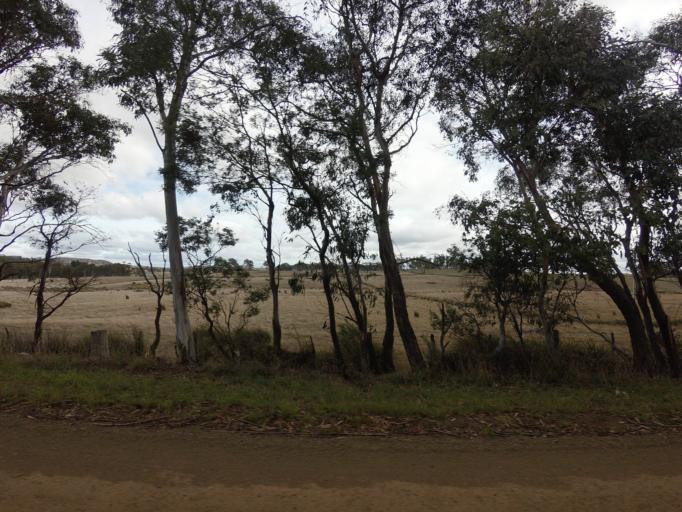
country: AU
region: Tasmania
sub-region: Brighton
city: Bridgewater
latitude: -42.4255
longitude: 147.4285
